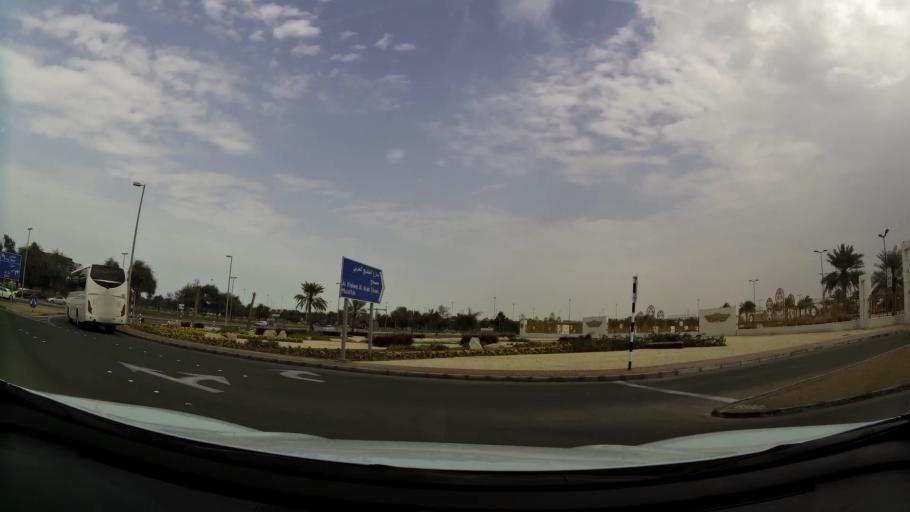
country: AE
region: Abu Dhabi
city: Abu Dhabi
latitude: 24.4172
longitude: 54.4740
